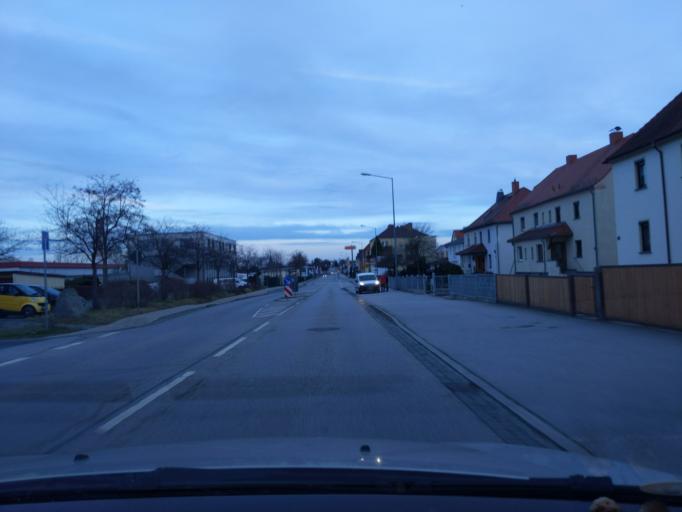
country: DE
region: Saxony
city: Bautzen
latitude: 51.1796
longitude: 14.3918
